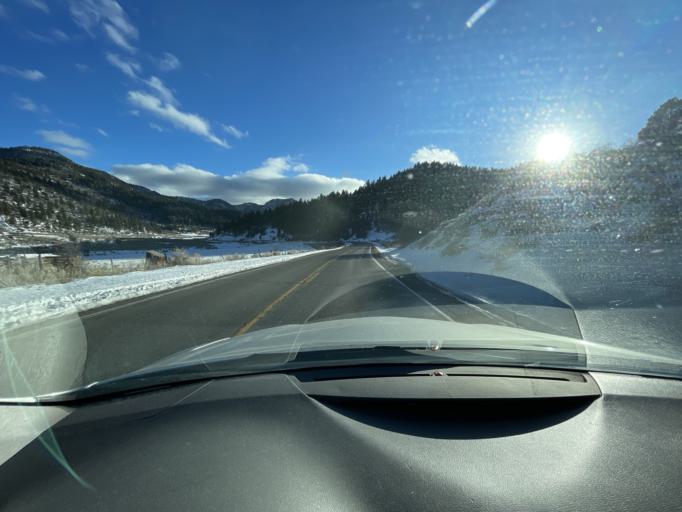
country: US
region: Colorado
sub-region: Mesa County
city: Loma
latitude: 39.6392
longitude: -108.7906
